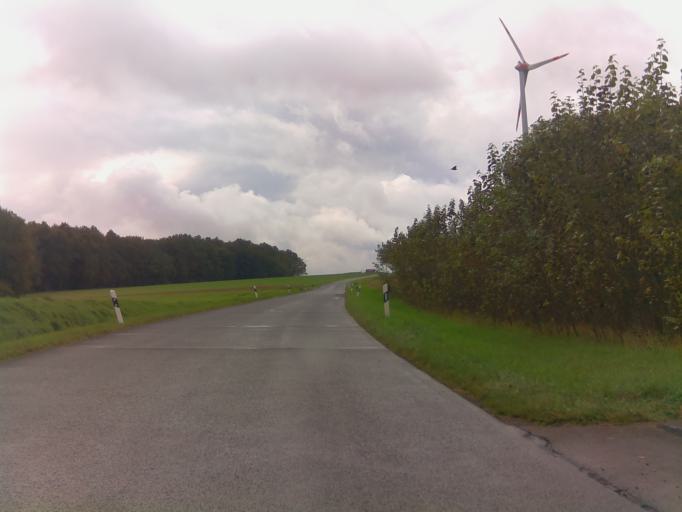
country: DE
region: Bavaria
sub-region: Upper Franconia
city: Priesendorf
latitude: 49.9149
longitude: 10.7424
